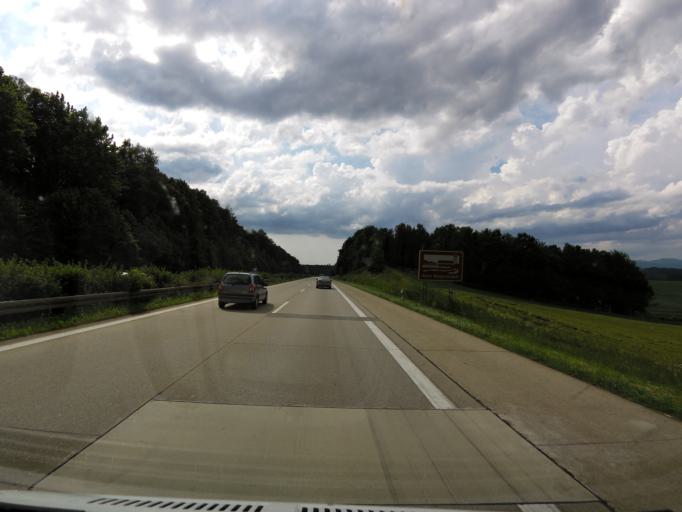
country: DE
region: Bavaria
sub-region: Lower Bavaria
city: Winzer
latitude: 48.7522
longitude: 13.0833
